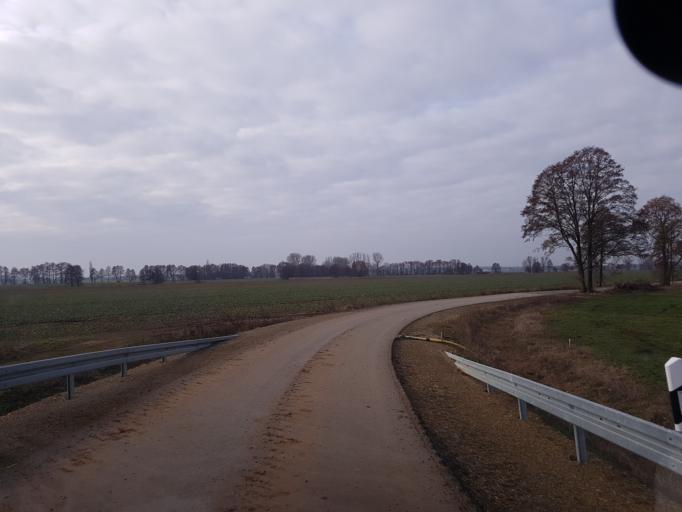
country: DE
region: Brandenburg
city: Schonewalde
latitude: 51.6680
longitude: 13.5833
